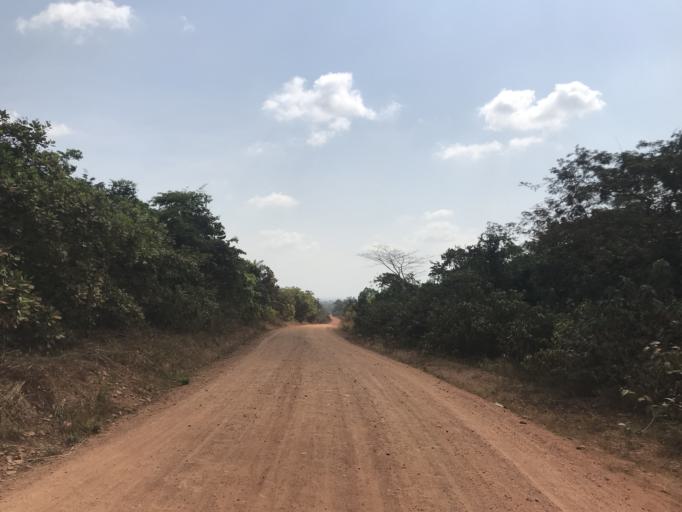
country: NG
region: Osun
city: Ifon
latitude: 7.8893
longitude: 4.4776
